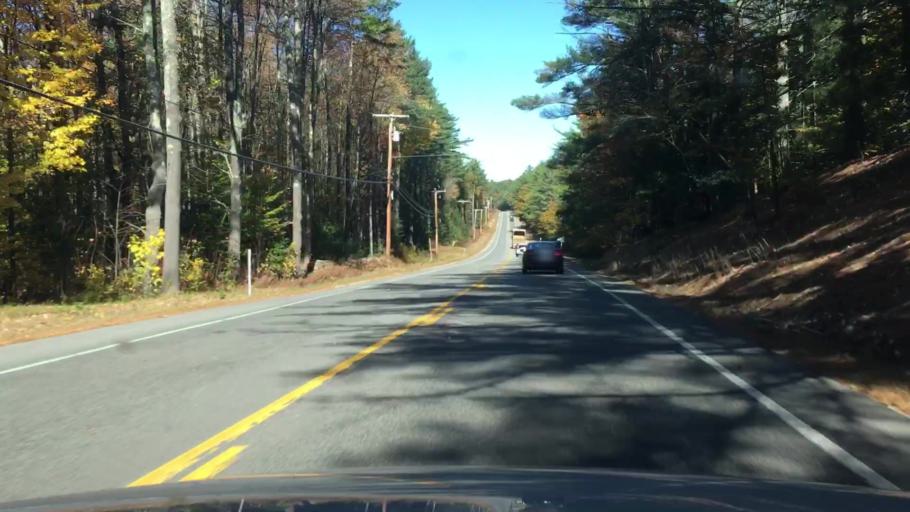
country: US
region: New Hampshire
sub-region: Carroll County
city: Ossipee
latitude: 43.7185
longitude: -71.1236
